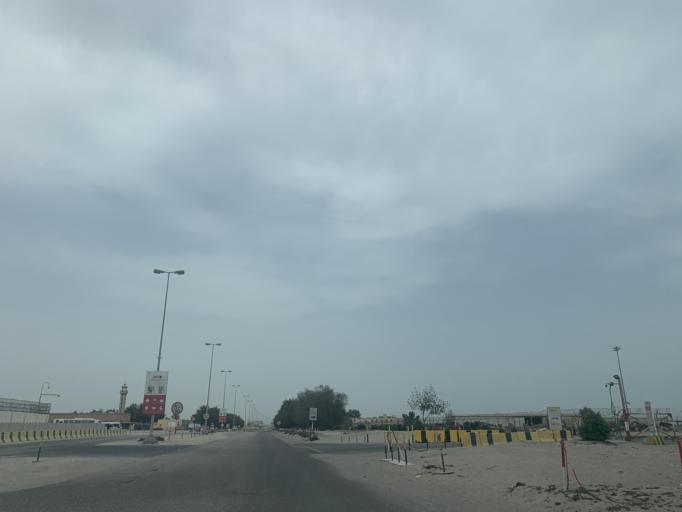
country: BH
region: Muharraq
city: Al Hadd
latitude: 26.1937
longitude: 50.6648
